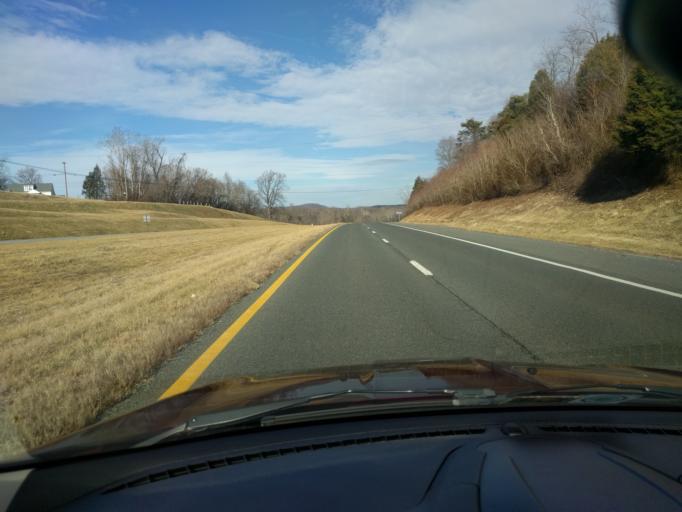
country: US
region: Virginia
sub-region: Amherst County
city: Madison Heights
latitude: 37.5026
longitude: -79.1236
